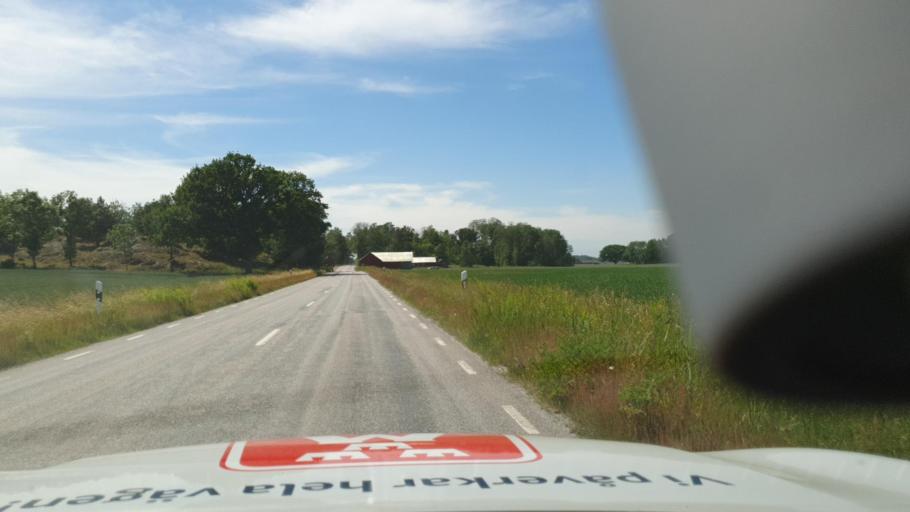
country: SE
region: Vaestra Goetaland
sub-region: Lidkopings Kommun
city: Lidkoping
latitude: 58.5114
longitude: 13.0437
